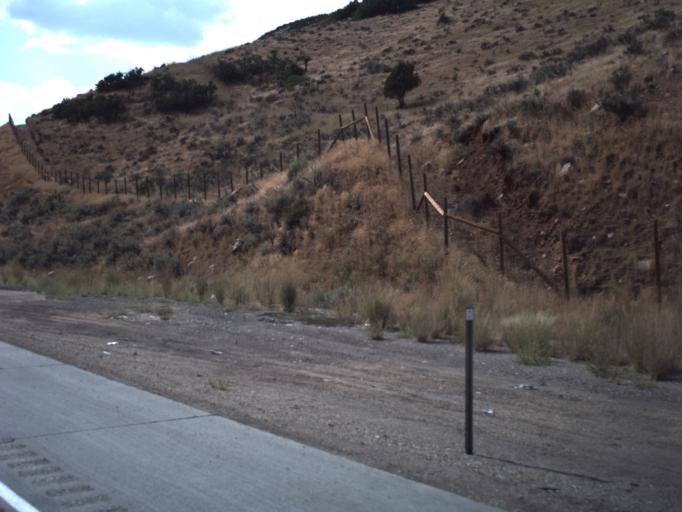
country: US
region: Utah
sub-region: Summit County
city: Snyderville
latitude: 40.7794
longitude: -111.4627
